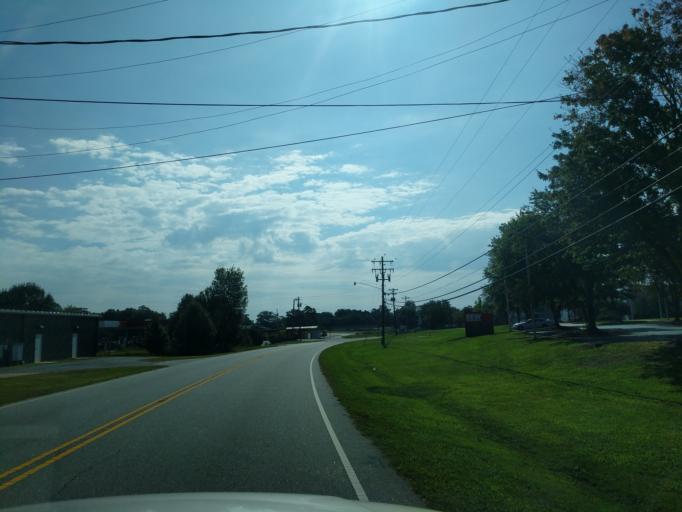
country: US
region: South Carolina
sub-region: Spartanburg County
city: Wellford
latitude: 34.9537
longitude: -82.1143
